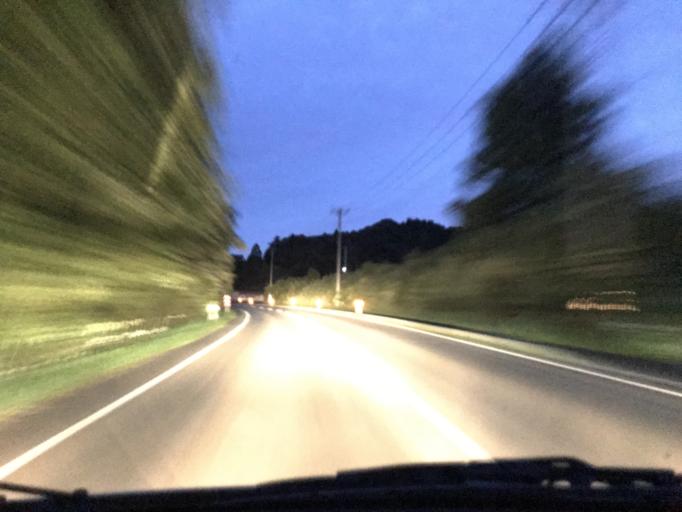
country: JP
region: Iwate
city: Kitakami
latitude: 39.2935
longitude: 141.1727
